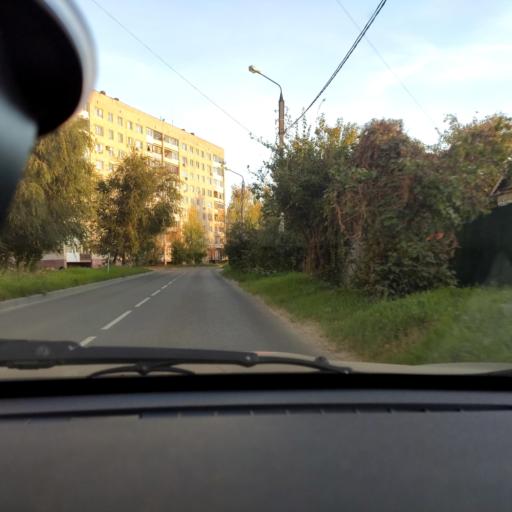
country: RU
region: Samara
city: Tol'yatti
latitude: 53.5078
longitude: 49.3983
